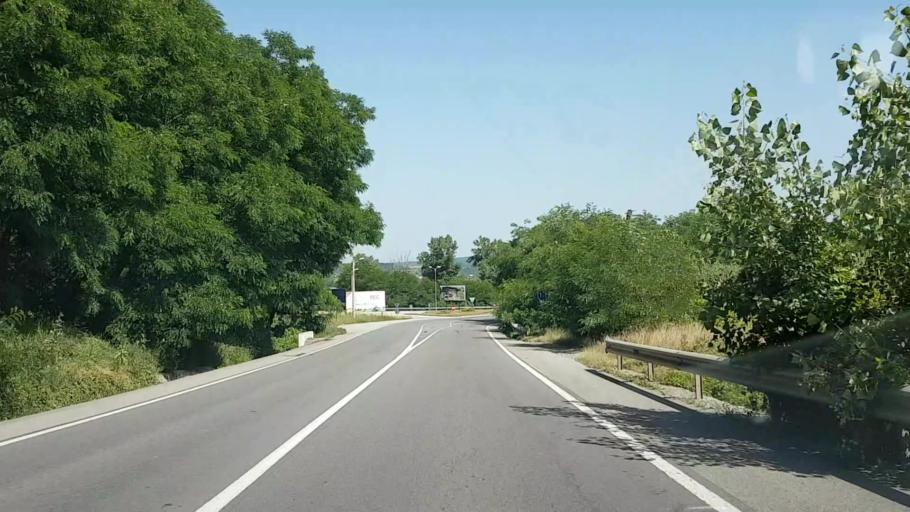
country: RO
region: Bistrita-Nasaud
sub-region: Comuna Beclean
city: Beclean
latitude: 47.1789
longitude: 24.1451
